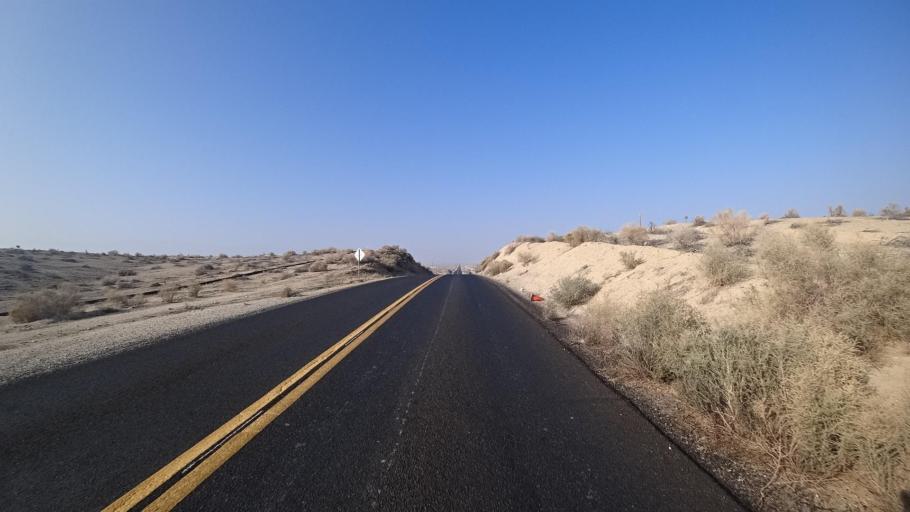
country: US
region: California
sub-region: Kern County
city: Ford City
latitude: 35.1806
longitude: -119.4675
